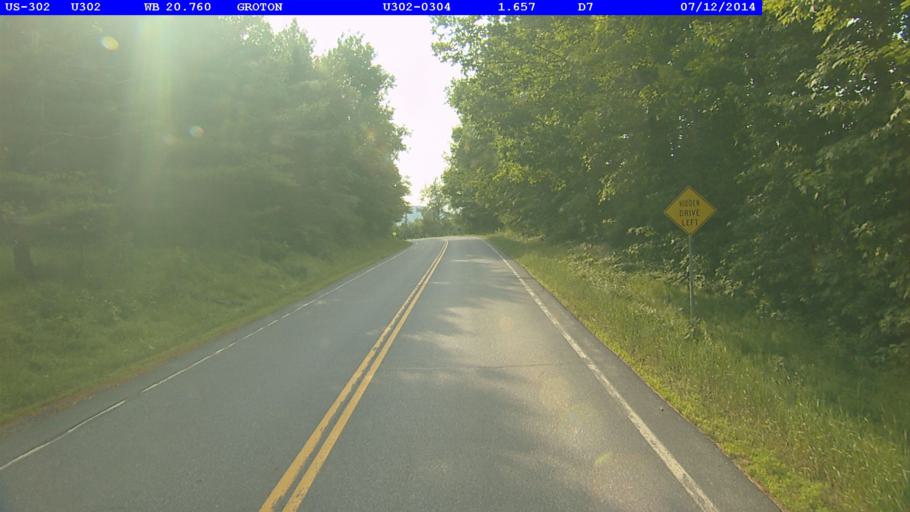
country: US
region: Vermont
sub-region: Washington County
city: Barre
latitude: 44.1986
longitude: -72.2742
